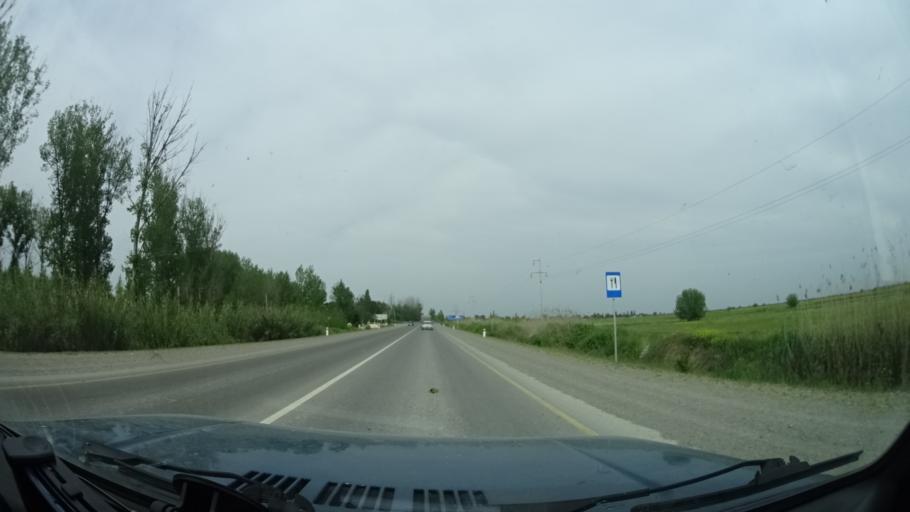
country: AZ
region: Imisli
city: Imishli
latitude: 39.7569
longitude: 47.9978
